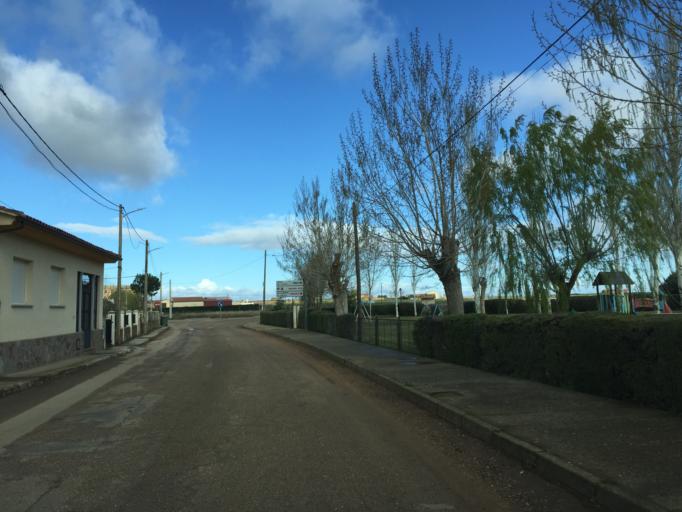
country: ES
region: Castille and Leon
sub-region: Provincia de Zamora
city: Manganeses de la Lampreana
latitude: 41.7524
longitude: -5.7139
